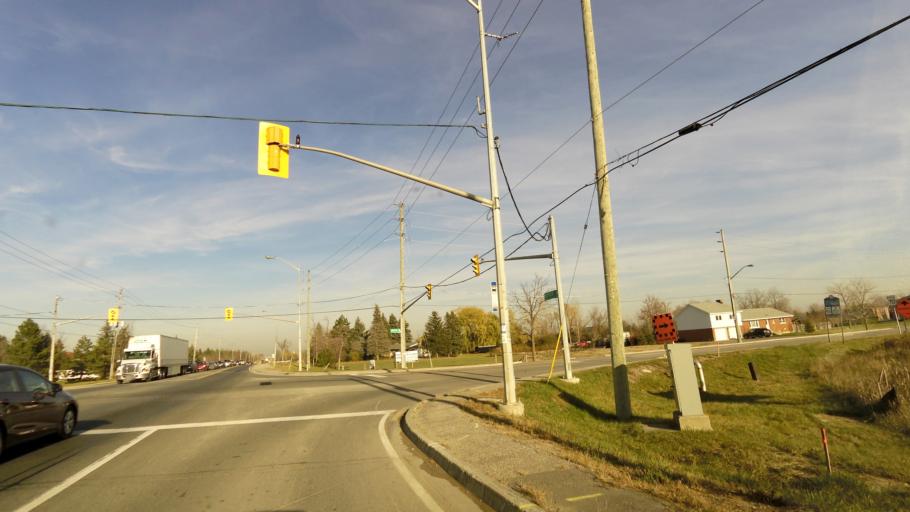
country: CA
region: Ontario
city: Brampton
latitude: 43.8003
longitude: -79.7491
